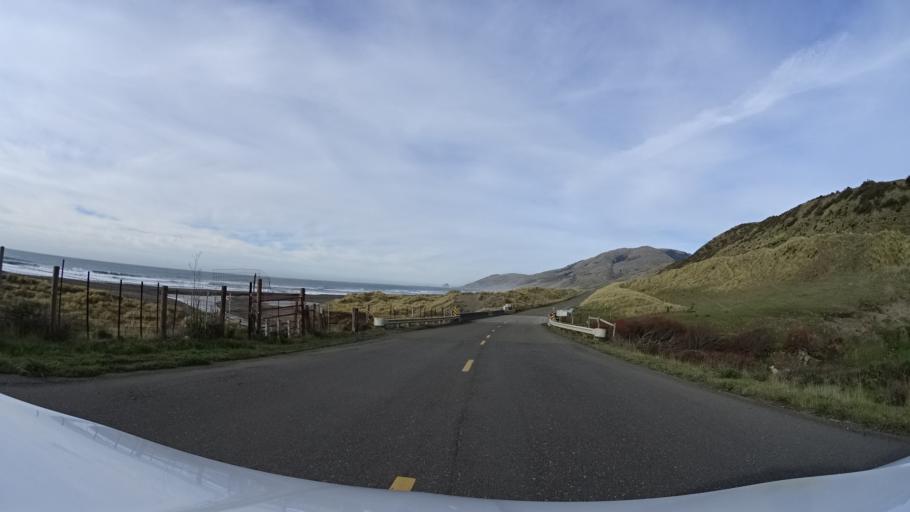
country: US
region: California
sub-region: Humboldt County
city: Ferndale
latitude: 40.3522
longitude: -124.3607
